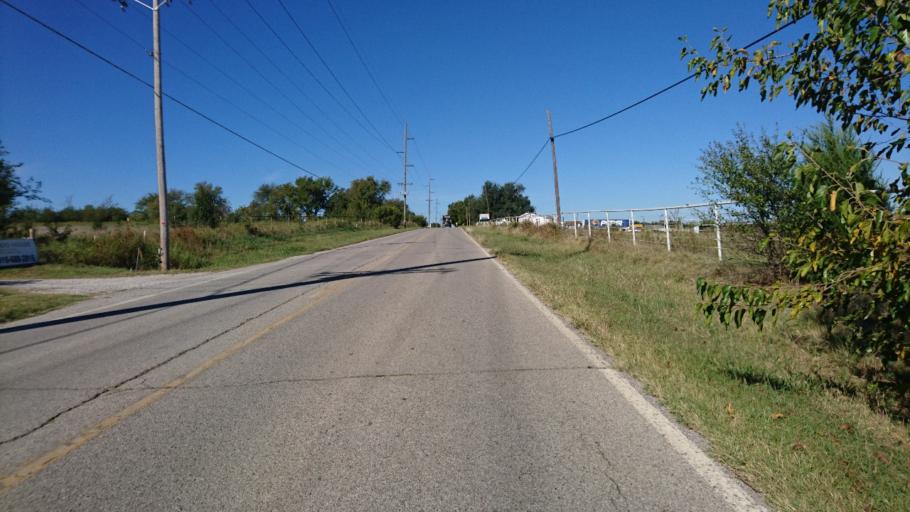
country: US
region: Oklahoma
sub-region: Rogers County
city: Catoosa
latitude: 36.1480
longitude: -95.7895
